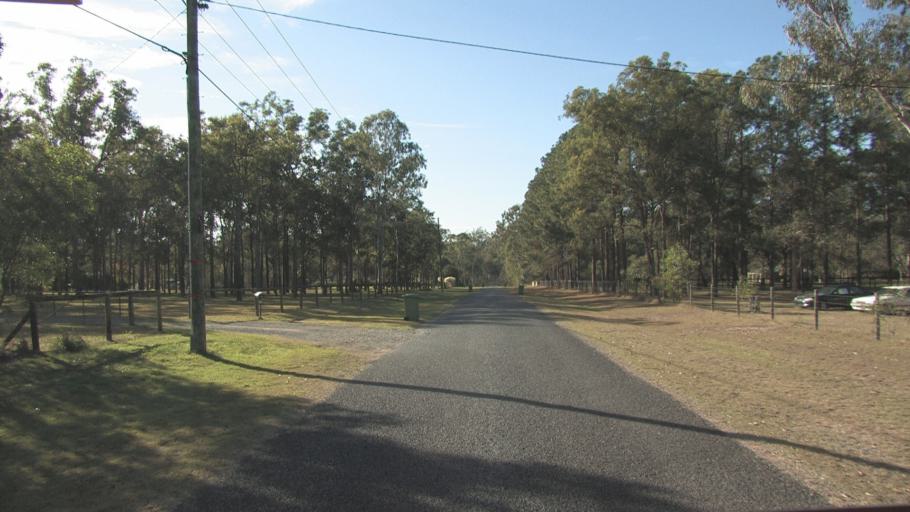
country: AU
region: Queensland
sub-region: Logan
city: North Maclean
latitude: -27.7613
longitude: 153.0049
